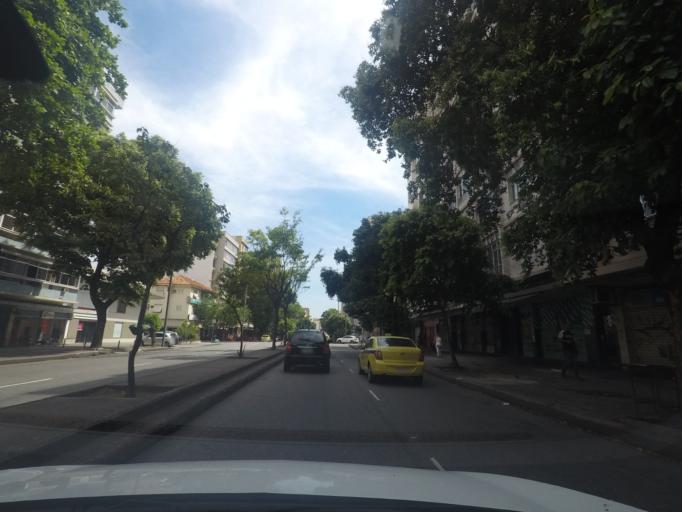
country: BR
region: Rio de Janeiro
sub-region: Rio De Janeiro
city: Rio de Janeiro
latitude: -22.9293
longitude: -43.2370
